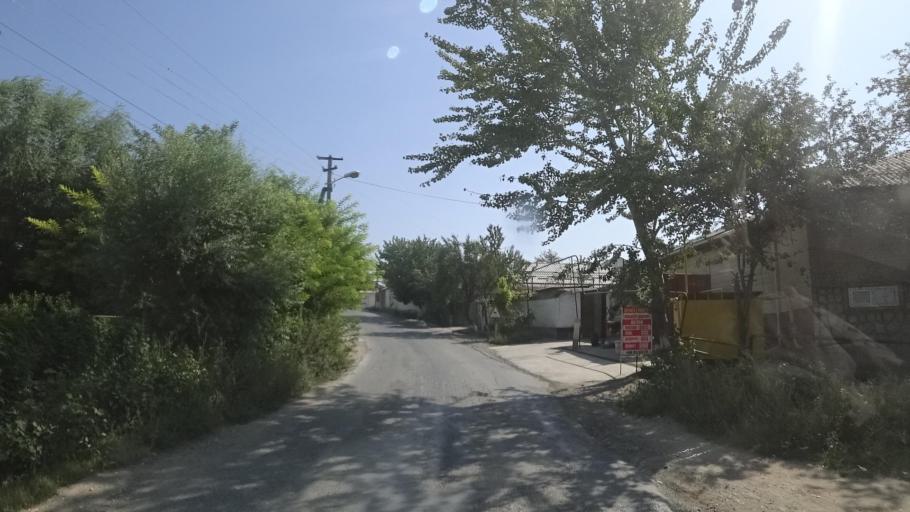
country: KG
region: Osh
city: Osh
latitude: 40.5202
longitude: 72.8191
